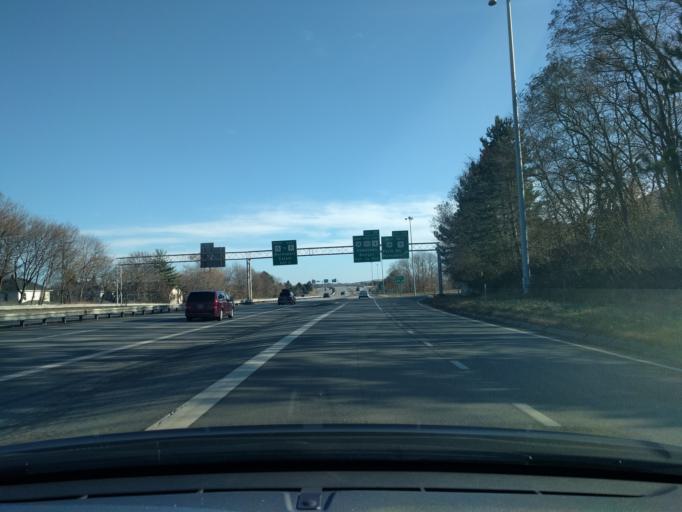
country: US
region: Maine
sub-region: Penobscot County
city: Bangor
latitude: 44.7870
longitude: -68.7834
